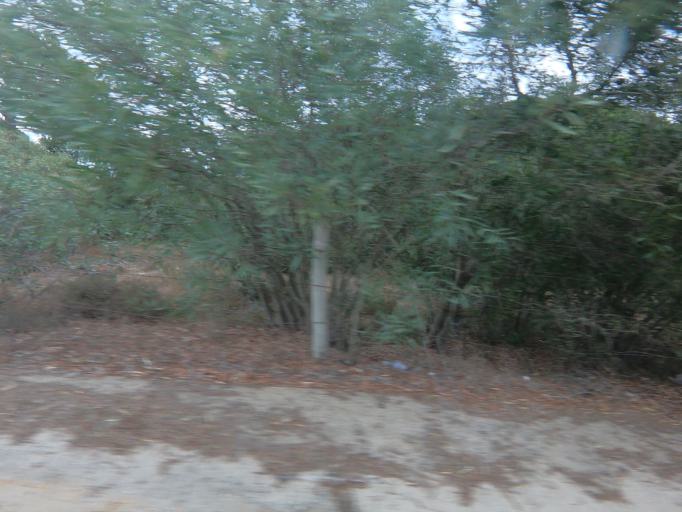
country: PT
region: Setubal
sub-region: Almada
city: Charneca
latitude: 38.5788
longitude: -9.1945
